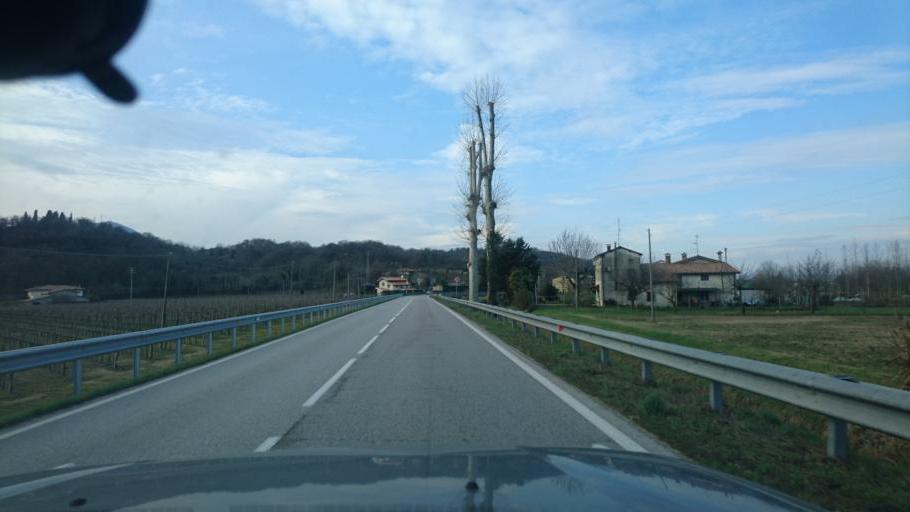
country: IT
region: Veneto
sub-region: Provincia di Padova
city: Bastia
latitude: 45.3947
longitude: 11.6788
